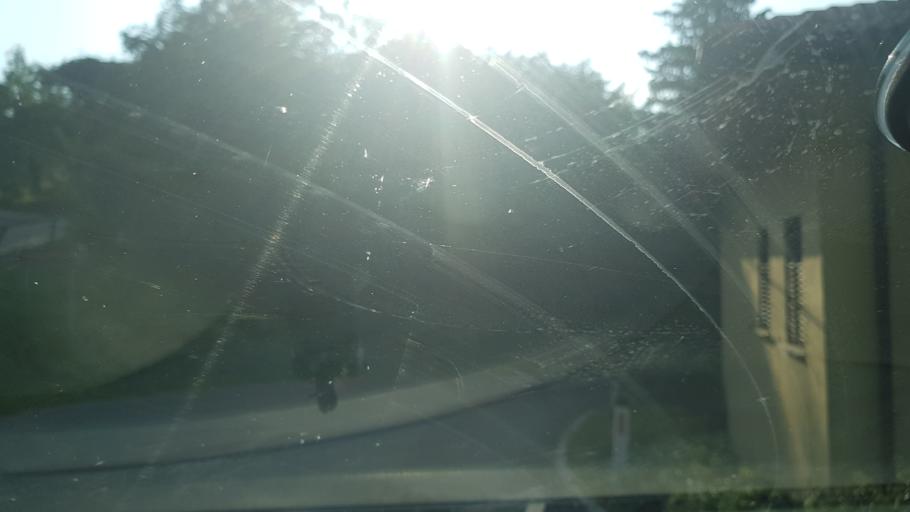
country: SI
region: Nova Gorica
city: Nova Gorica
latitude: 45.9467
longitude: 13.6434
